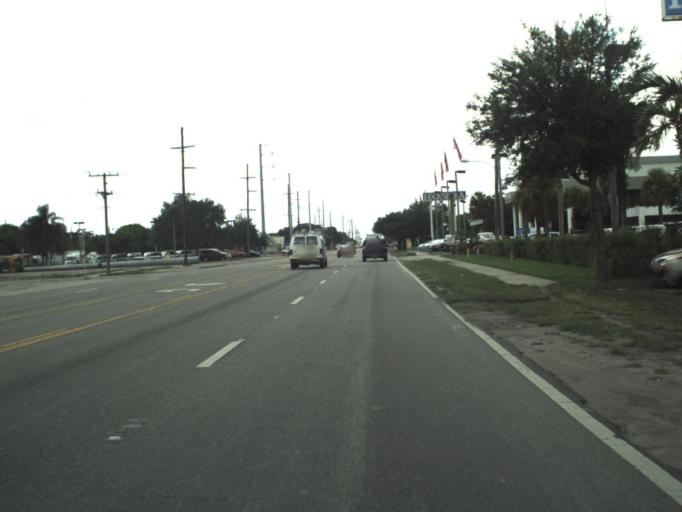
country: US
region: Florida
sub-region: Broward County
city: Pembroke Pines
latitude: 26.0238
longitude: -80.2082
